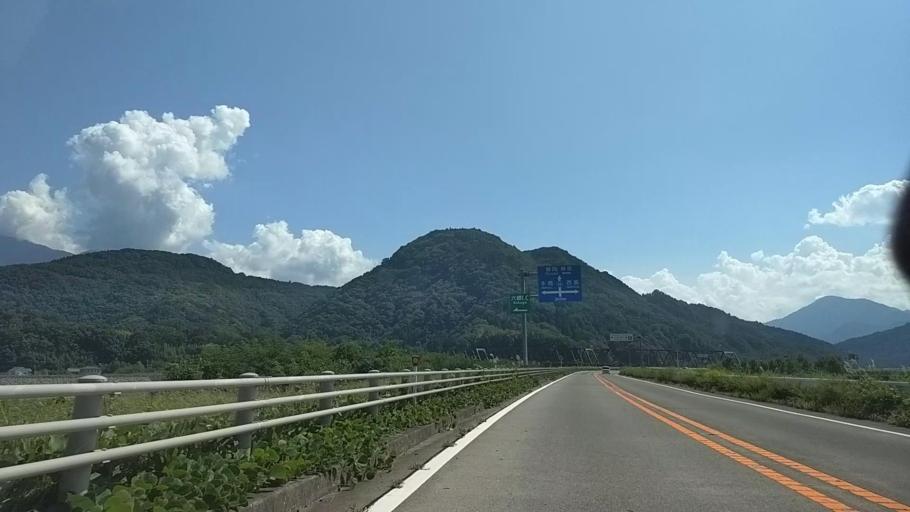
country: JP
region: Yamanashi
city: Ryuo
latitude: 35.4886
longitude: 138.4537
